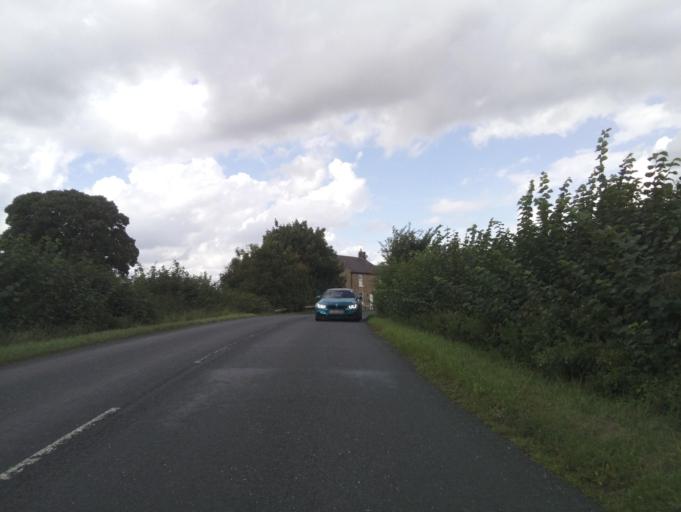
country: GB
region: England
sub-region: North Yorkshire
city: Bedale
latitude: 54.2444
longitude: -1.6906
